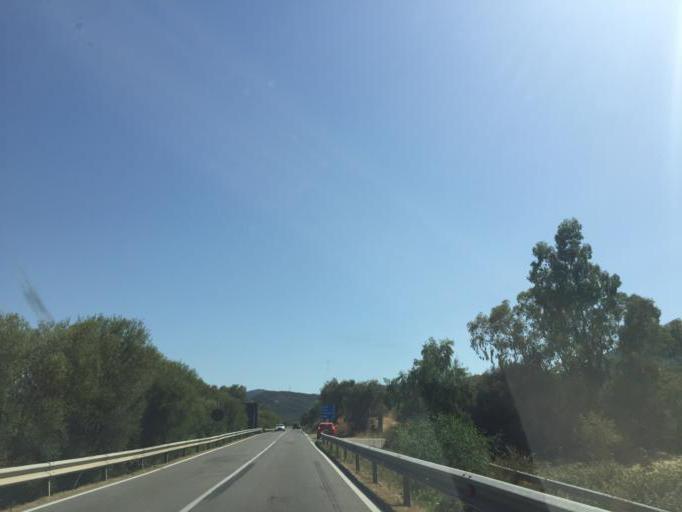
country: IT
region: Sardinia
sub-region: Provincia di Olbia-Tempio
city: San Teodoro
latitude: 40.7595
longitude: 9.6528
